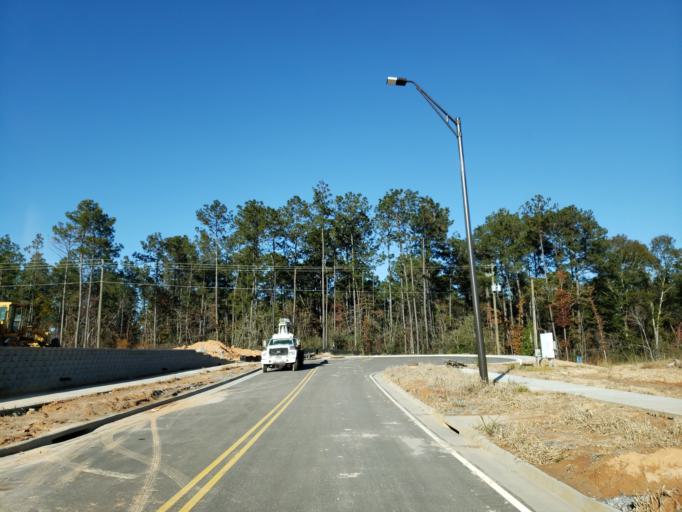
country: US
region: Mississippi
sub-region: Forrest County
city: Hattiesburg
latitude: 31.2828
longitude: -89.3227
